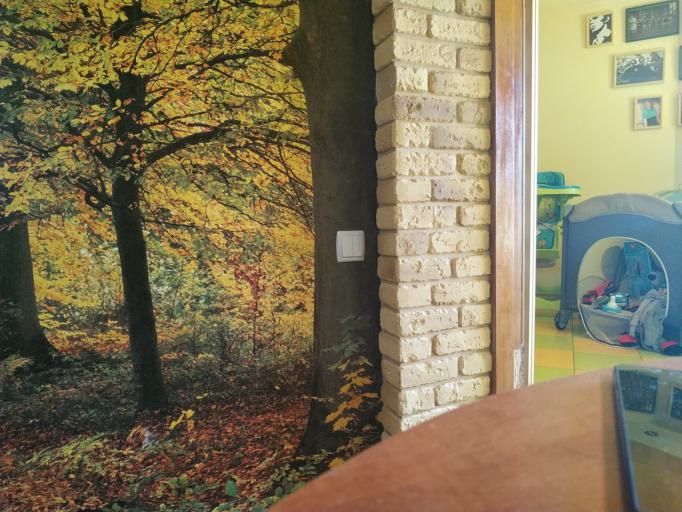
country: RU
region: Tverskaya
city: Torzhok
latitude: 57.0740
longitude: 35.0073
